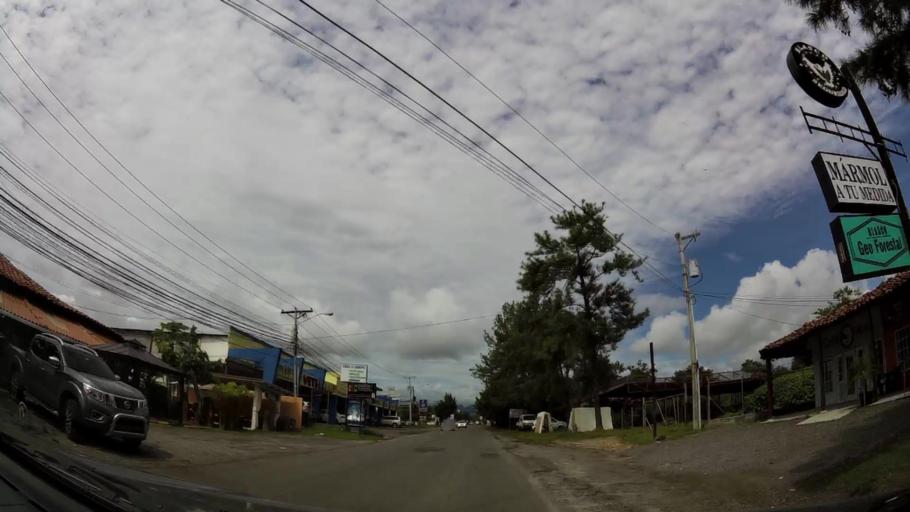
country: PA
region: Panama
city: Nueva Gorgona
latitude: 8.5401
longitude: -79.9099
